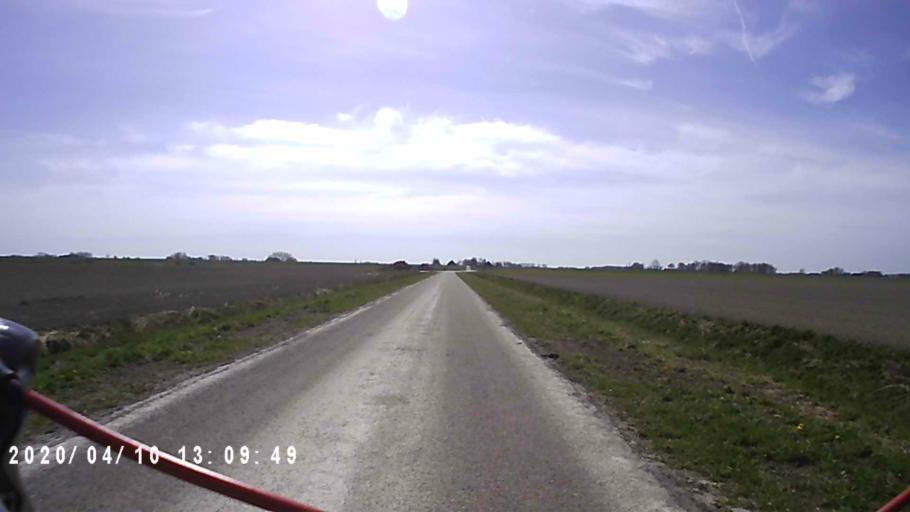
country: NL
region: Groningen
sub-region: Gemeente De Marne
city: Ulrum
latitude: 53.4121
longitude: 6.4196
